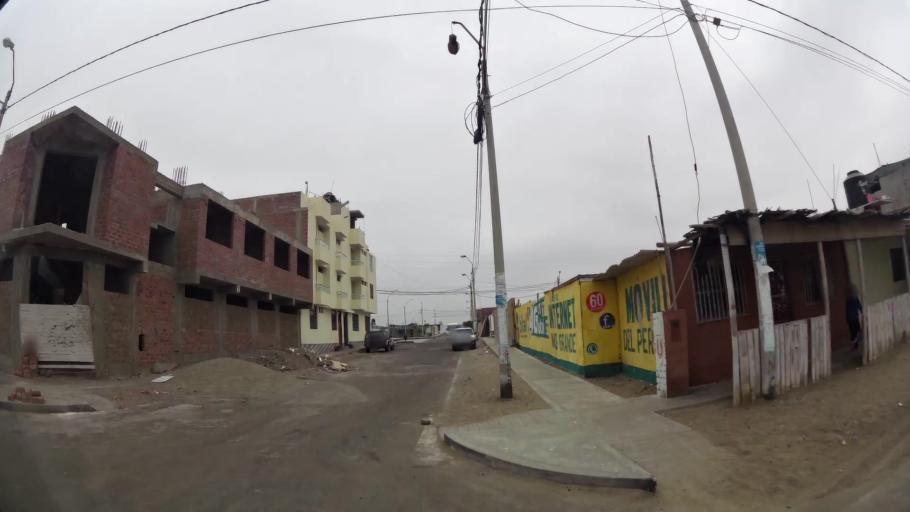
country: PE
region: Ica
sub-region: Provincia de Pisco
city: Paracas
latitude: -13.8364
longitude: -76.2487
